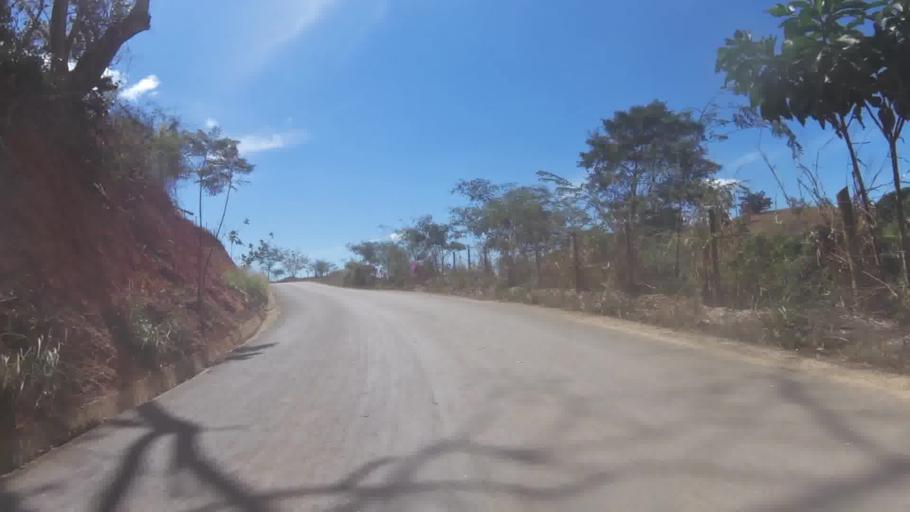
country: BR
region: Espirito Santo
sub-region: Cachoeiro De Itapemirim
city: Cachoeiro de Itapemirim
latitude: -20.9410
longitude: -41.2213
